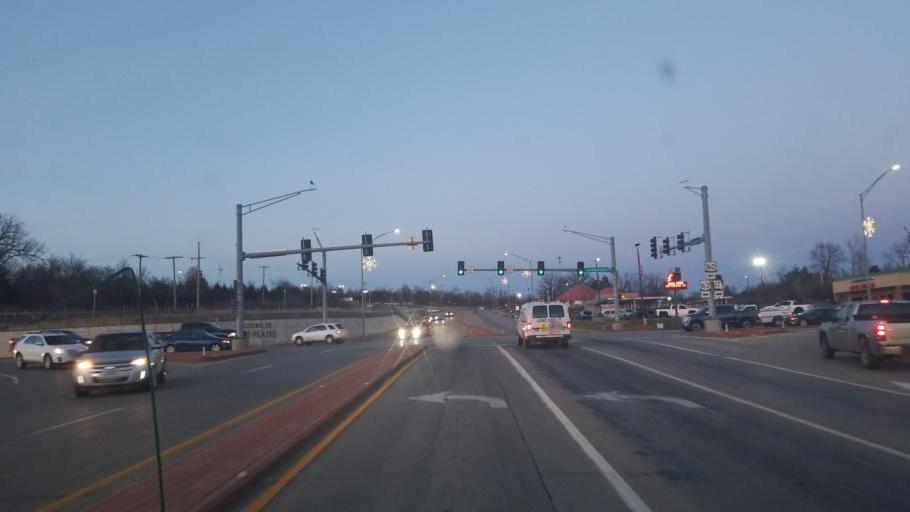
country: US
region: Missouri
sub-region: Howell County
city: West Plains
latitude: 36.7176
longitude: -91.8729
